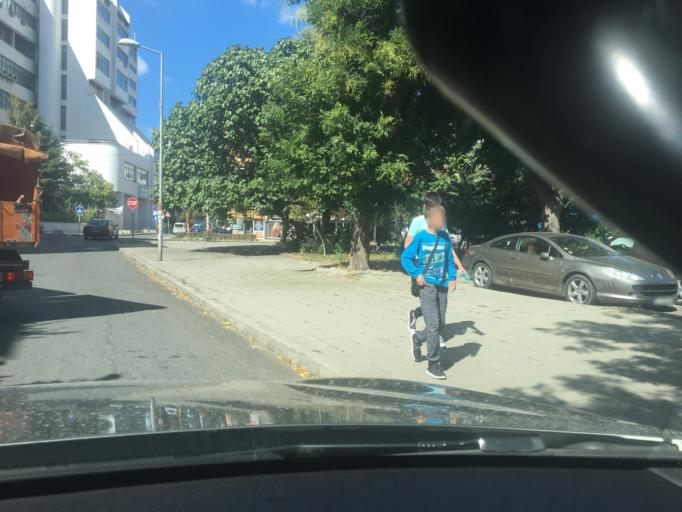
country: BG
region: Burgas
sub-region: Obshtina Burgas
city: Burgas
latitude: 42.5028
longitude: 27.4717
